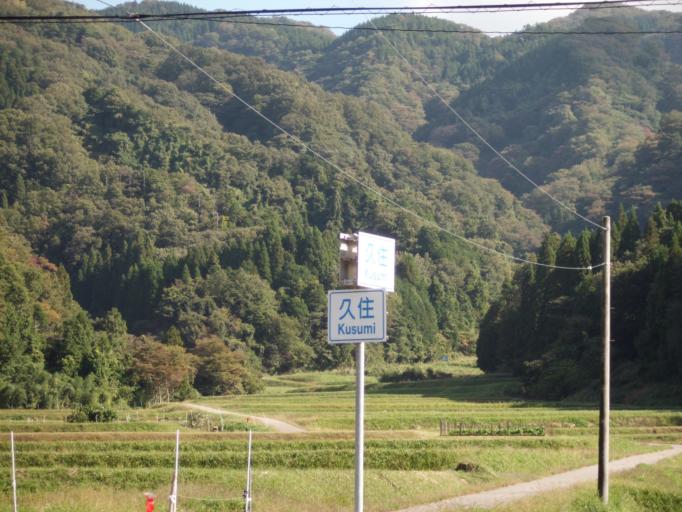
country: JP
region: Kyoto
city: Miyazu
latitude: 35.6157
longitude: 135.1305
